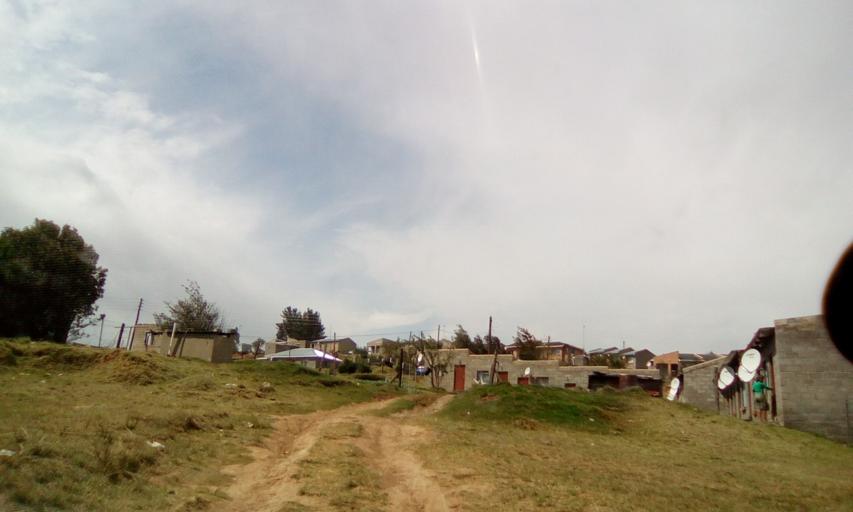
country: LS
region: Qacha's Nek
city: Qacha's Nek
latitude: -30.1150
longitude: 28.6799
